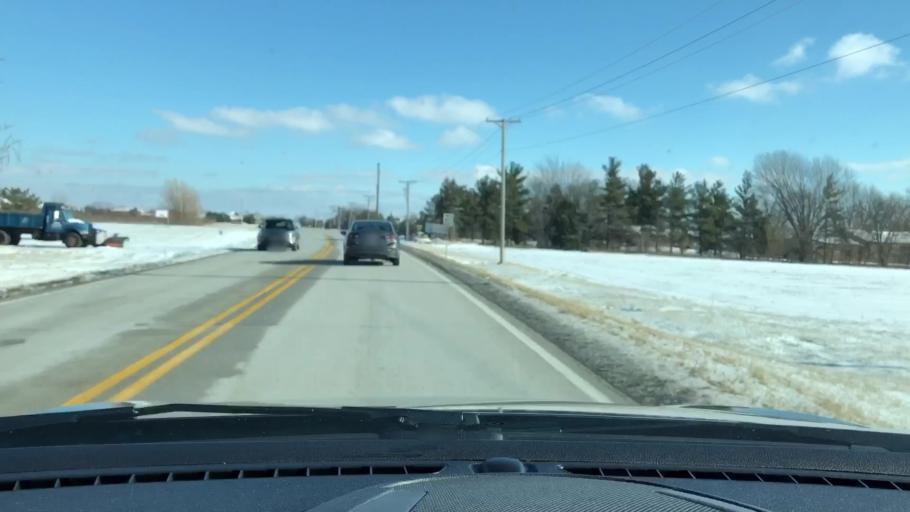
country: US
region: Illinois
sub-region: Will County
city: Mokena
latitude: 41.4837
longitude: -87.9055
